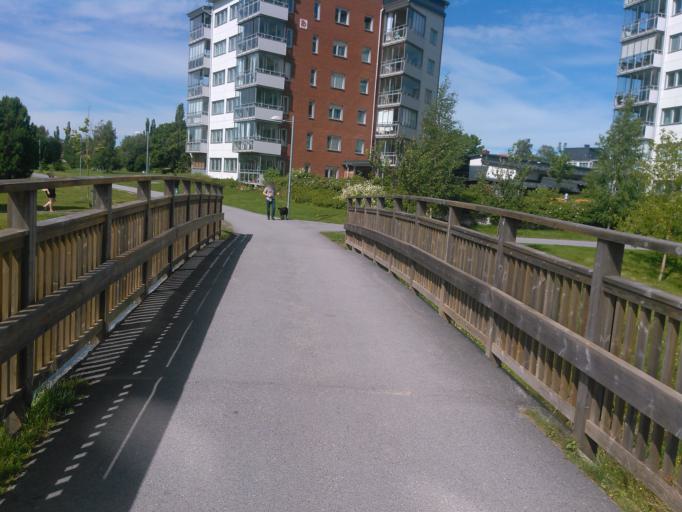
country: SE
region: Vaesterbotten
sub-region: Umea Kommun
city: Umea
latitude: 63.8163
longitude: 20.2904
